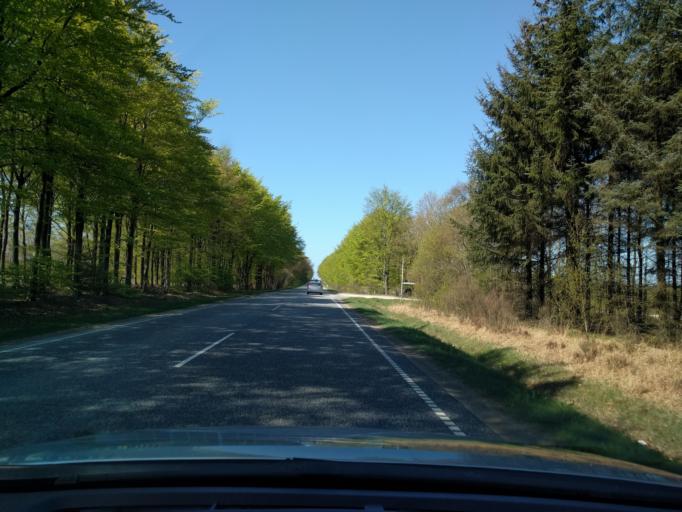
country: DK
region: Central Jutland
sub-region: Ringkobing-Skjern Kommune
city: Skjern
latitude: 56.0835
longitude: 8.4361
